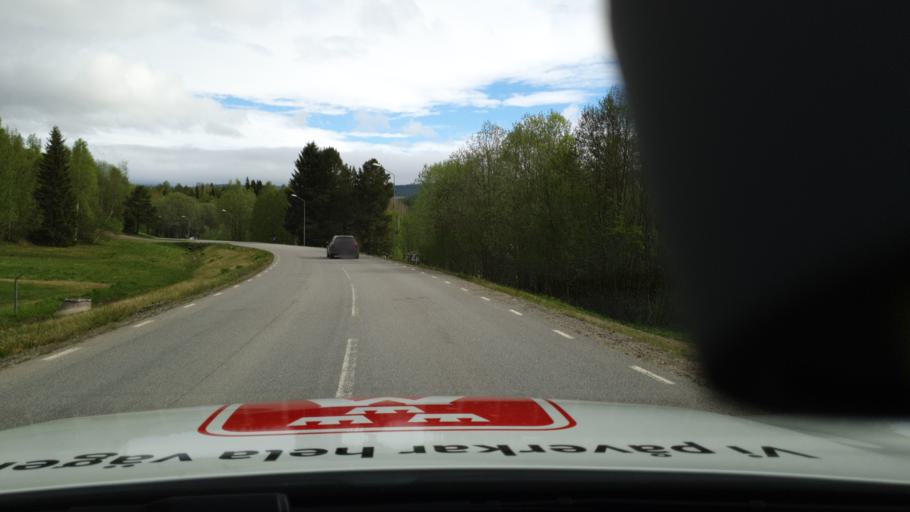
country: NO
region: Nord-Trondelag
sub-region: Lierne
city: Sandvika
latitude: 64.4931
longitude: 14.1393
